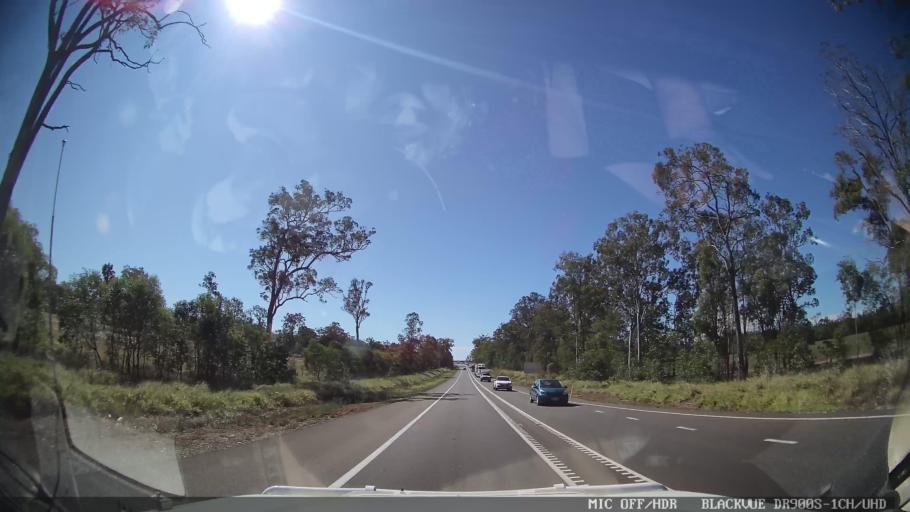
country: AU
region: Queensland
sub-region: Fraser Coast
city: Maryborough
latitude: -25.6507
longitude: 152.6331
